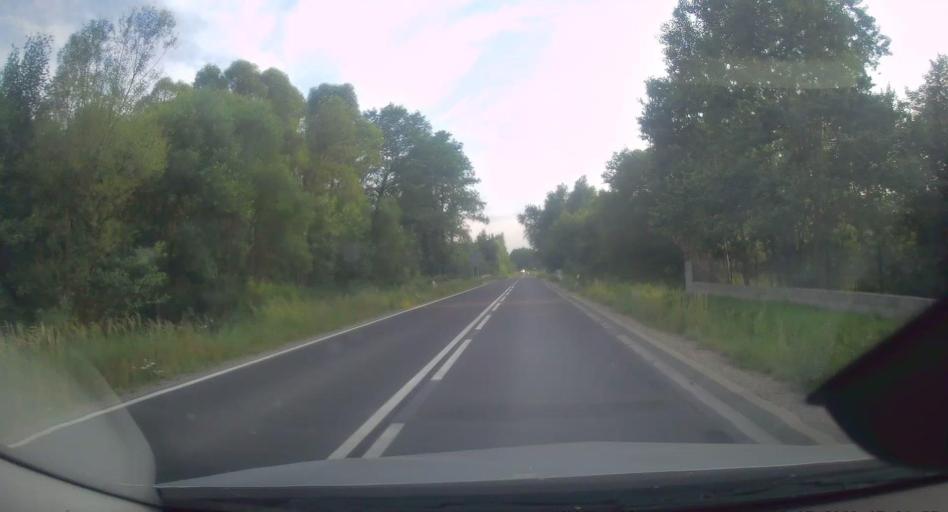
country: PL
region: Lesser Poland Voivodeship
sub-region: Powiat brzeski
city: Przyborow
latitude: 50.0284
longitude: 20.6373
